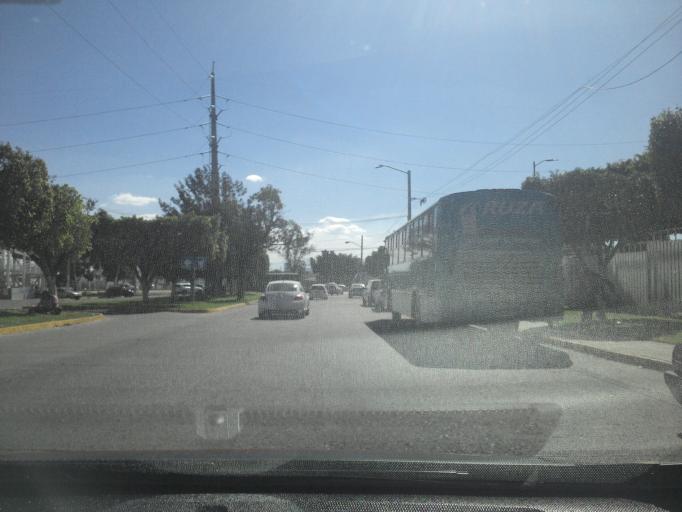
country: MX
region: Jalisco
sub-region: Zapopan
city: Zapopan
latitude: 20.7412
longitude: -103.3996
